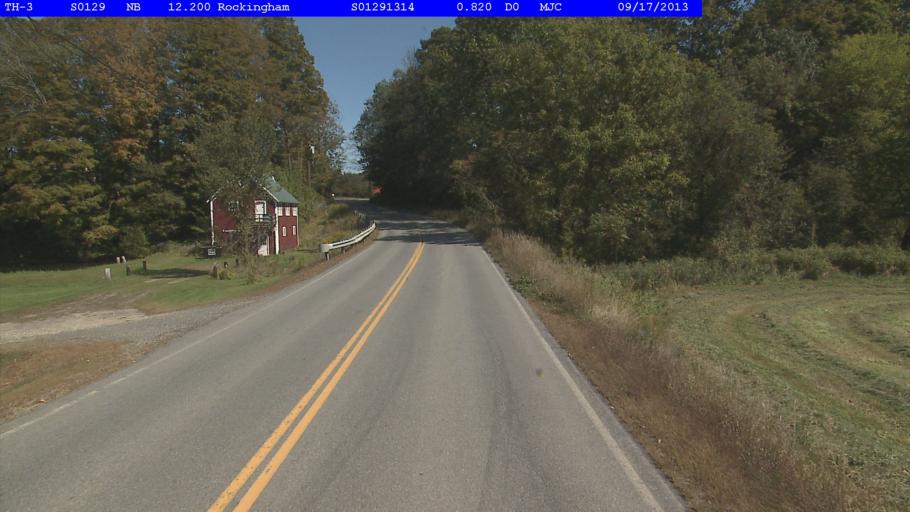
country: US
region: Vermont
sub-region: Windham County
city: Rockingham
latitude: 43.1332
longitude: -72.5144
